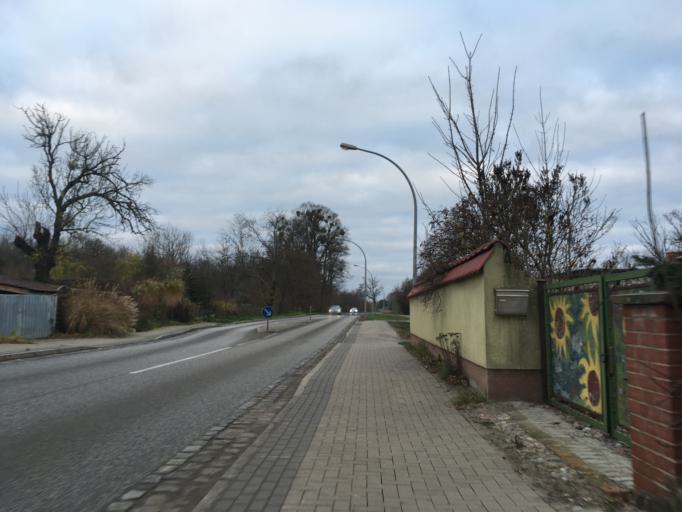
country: DE
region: Brandenburg
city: Seelow
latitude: 52.5748
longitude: 14.3490
